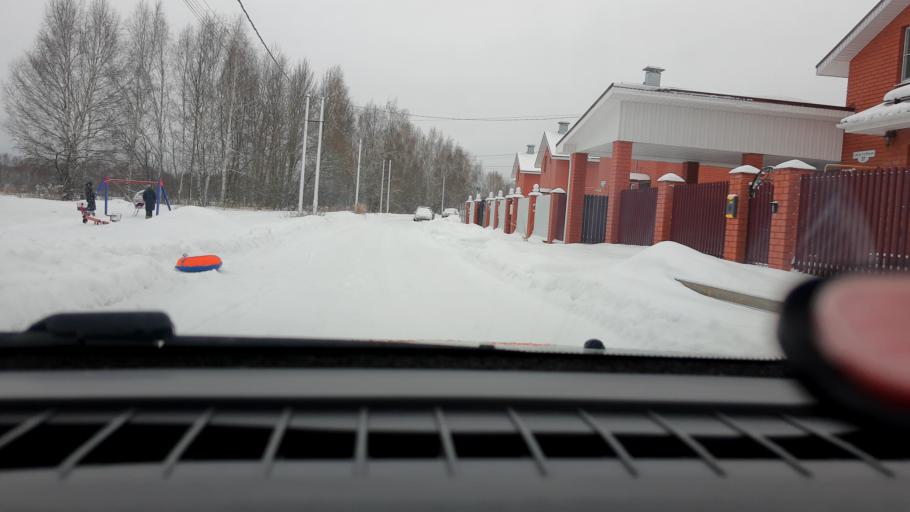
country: RU
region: Nizjnij Novgorod
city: Afonino
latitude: 56.1993
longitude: 44.0677
